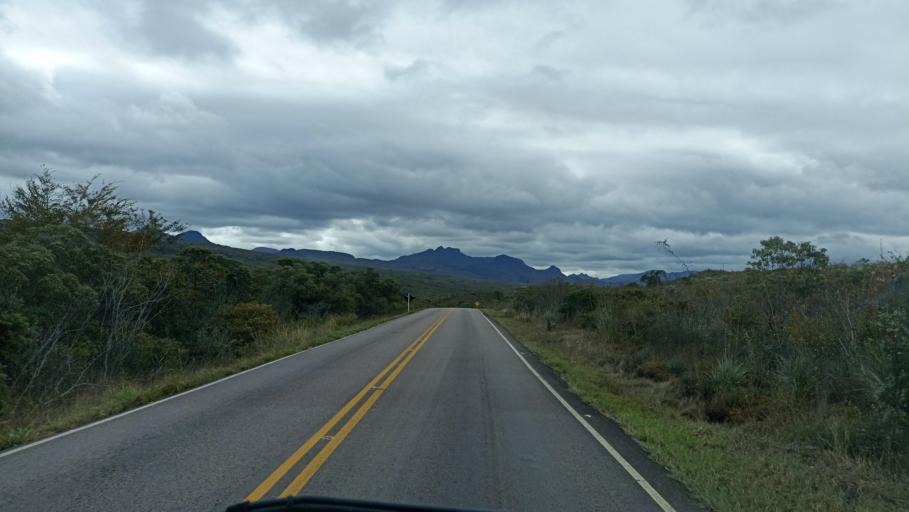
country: BR
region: Bahia
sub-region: Andarai
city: Vera Cruz
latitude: -12.9916
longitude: -41.3466
